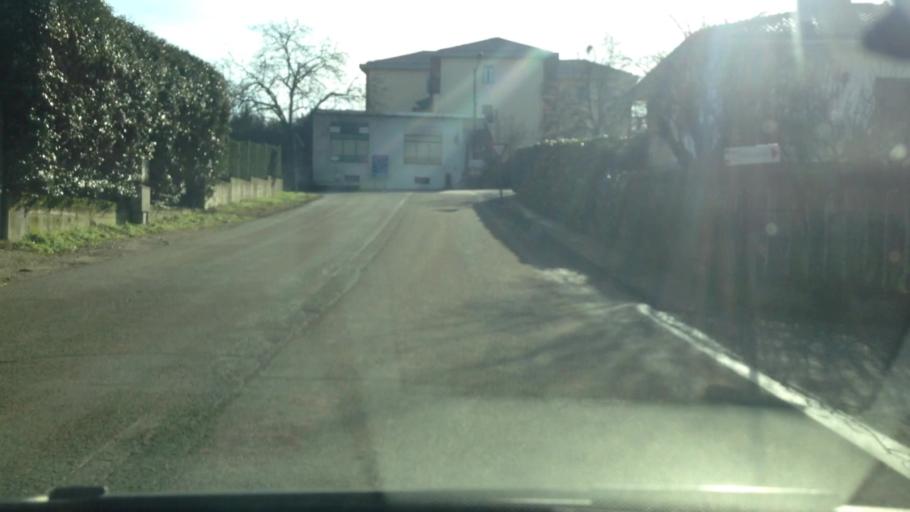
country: IT
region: Piedmont
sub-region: Provincia di Alessandria
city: Masio
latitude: 44.8712
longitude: 8.4108
